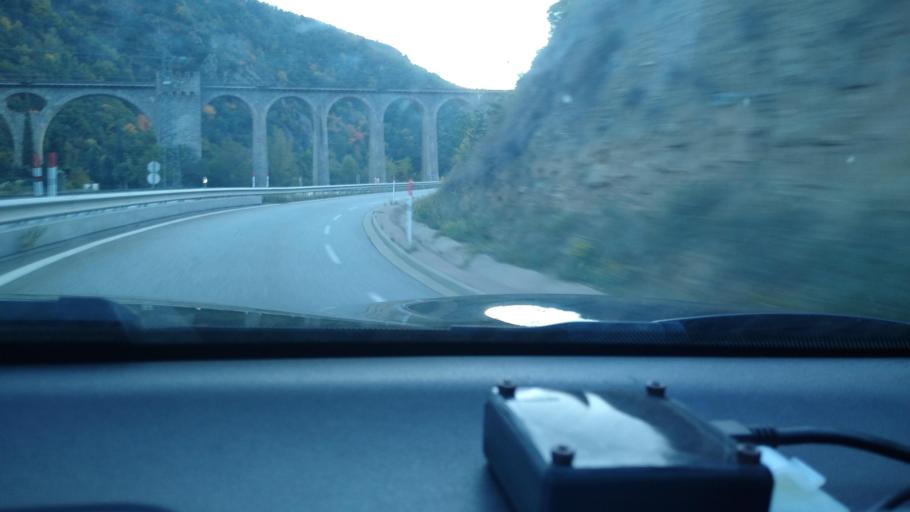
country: FR
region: Languedoc-Roussillon
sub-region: Departement des Pyrenees-Orientales
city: Vernet-les-Bains
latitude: 42.5190
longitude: 2.2037
